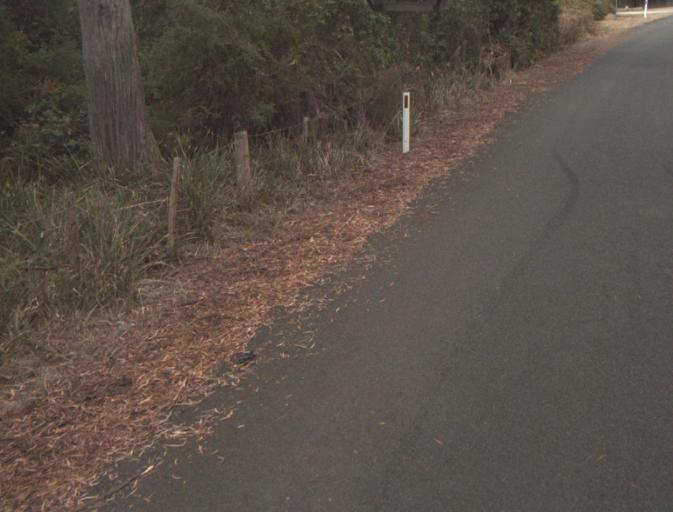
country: AU
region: Tasmania
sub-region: Launceston
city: Mayfield
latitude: -41.2823
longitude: 147.0410
